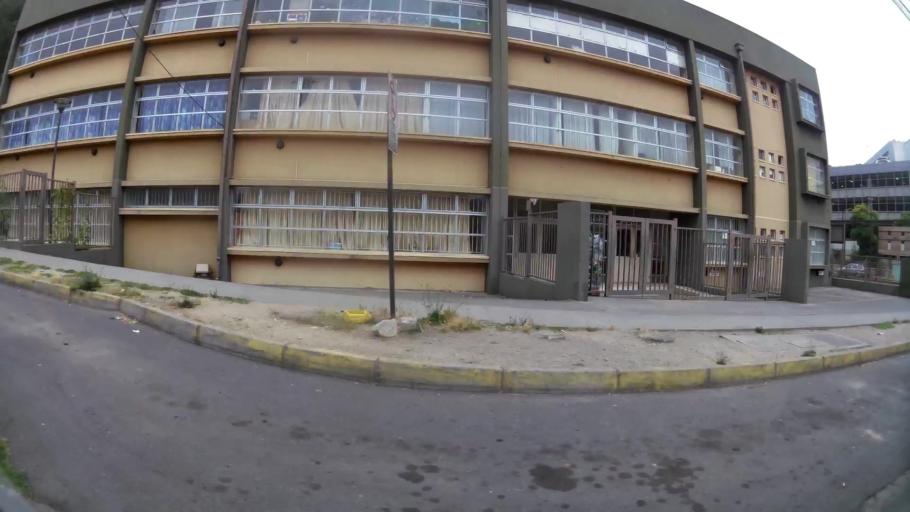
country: CL
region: Biobio
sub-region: Provincia de Concepcion
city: Concepcion
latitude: -36.8238
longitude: -73.0361
